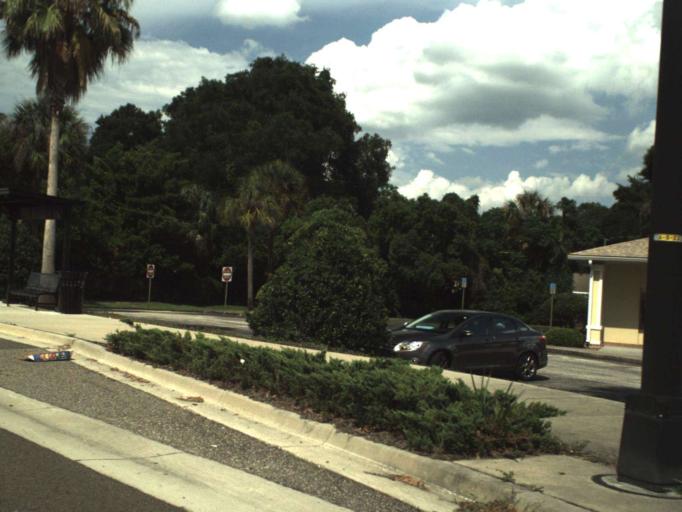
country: US
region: Florida
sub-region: Seminole County
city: Fern Park
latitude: 28.6435
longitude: -81.3539
